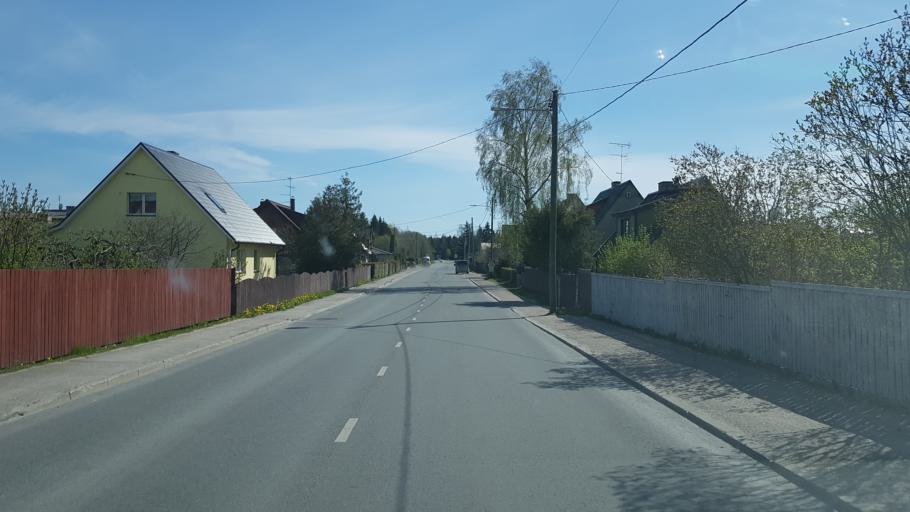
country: EE
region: Harju
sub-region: Keila linn
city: Keila
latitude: 59.3026
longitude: 24.4255
